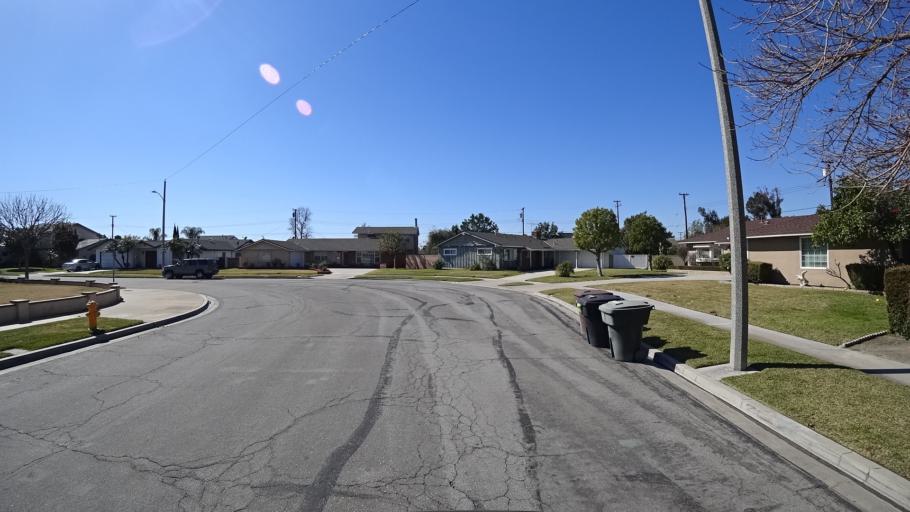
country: US
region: California
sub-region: Orange County
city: Orange
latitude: 33.8240
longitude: -117.8741
